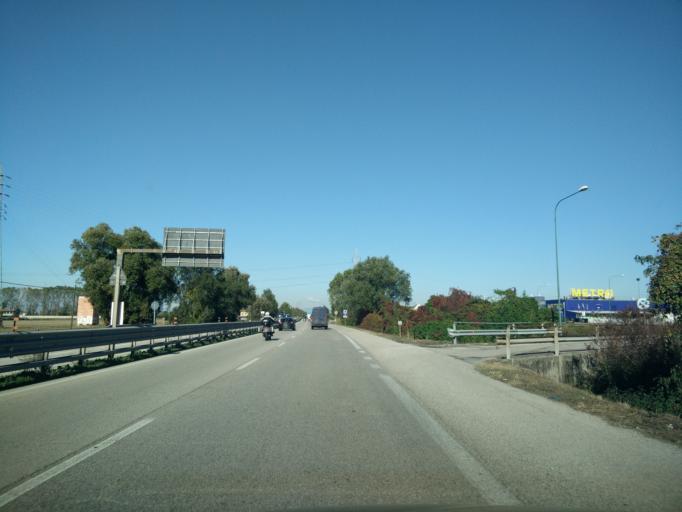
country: IT
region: Veneto
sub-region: Provincia di Venezia
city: Mestre
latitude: 45.4526
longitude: 12.2081
